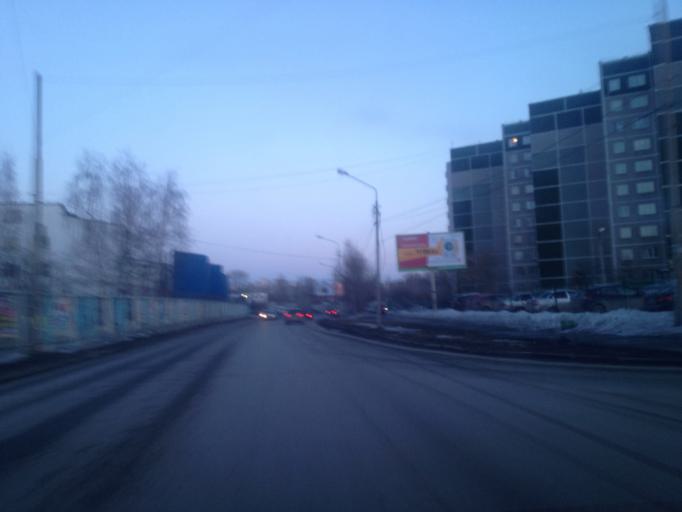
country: RU
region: Sverdlovsk
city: Yekaterinburg
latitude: 56.7938
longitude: 60.6354
